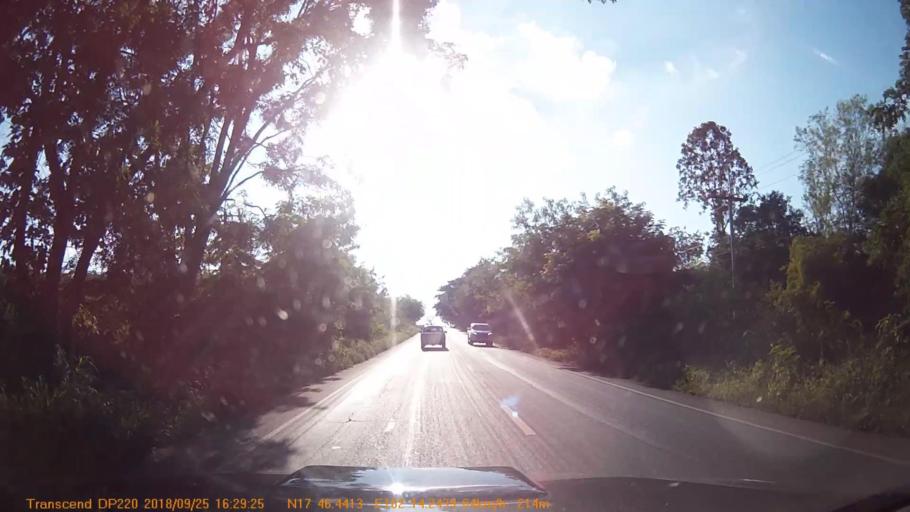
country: TH
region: Changwat Udon Thani
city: Nam Som
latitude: 17.7740
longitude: 102.2373
